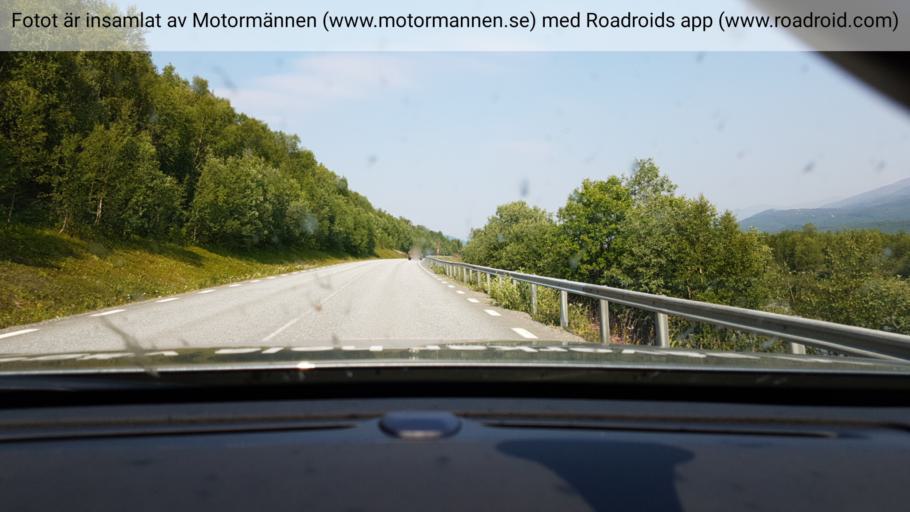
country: NO
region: Nordland
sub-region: Rana
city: Mo i Rana
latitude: 65.7327
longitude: 15.1494
